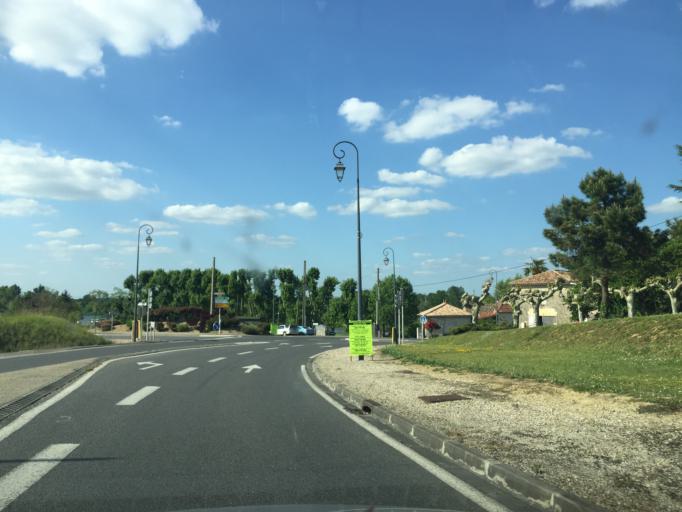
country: FR
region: Aquitaine
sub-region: Departement de la Gironde
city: Sainte-Terre
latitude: 44.8131
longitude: -0.1417
